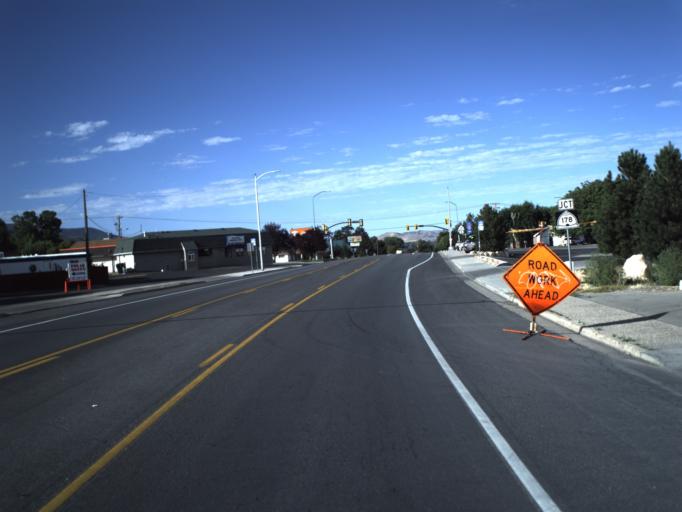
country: US
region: Utah
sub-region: Utah County
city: Payson
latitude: 40.0327
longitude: -111.7346
